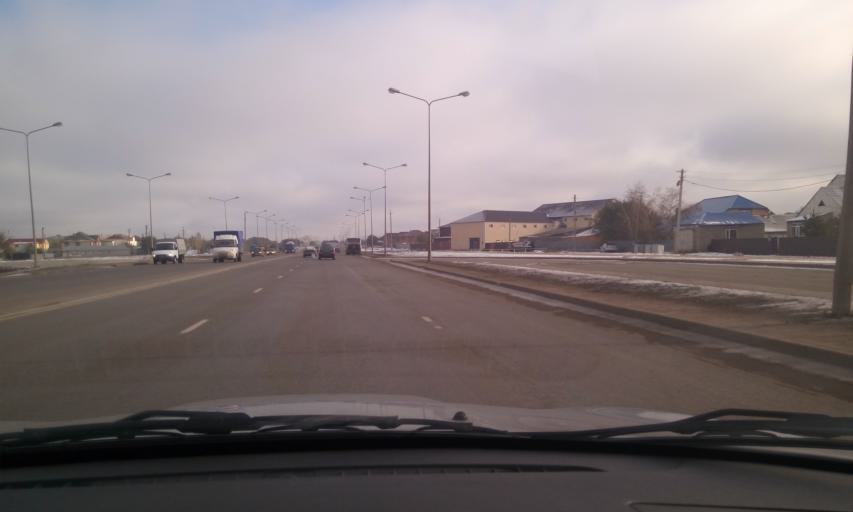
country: KZ
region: Astana Qalasy
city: Astana
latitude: 51.1318
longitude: 71.5073
